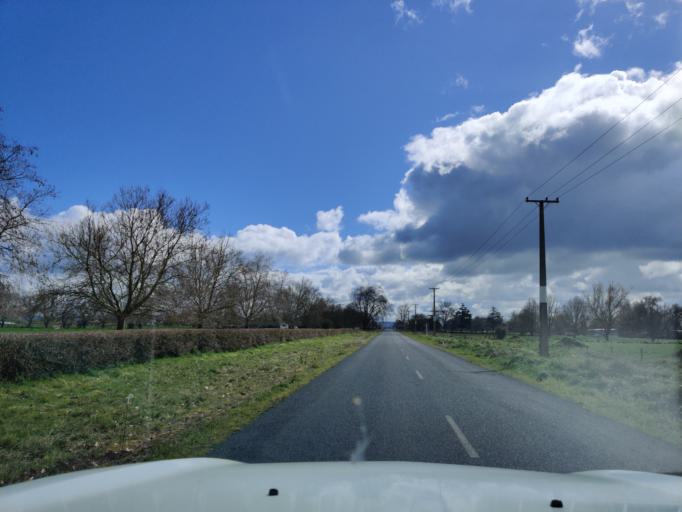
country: NZ
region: Waikato
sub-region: Waikato District
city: Ngaruawahia
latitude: -37.6152
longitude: 175.3141
